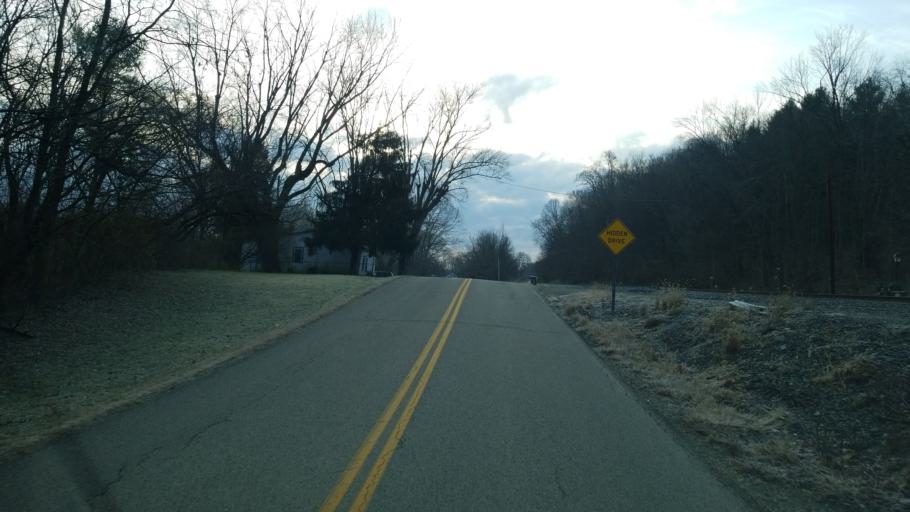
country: US
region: Ohio
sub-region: Ross County
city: Chillicothe
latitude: 39.2567
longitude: -82.9128
